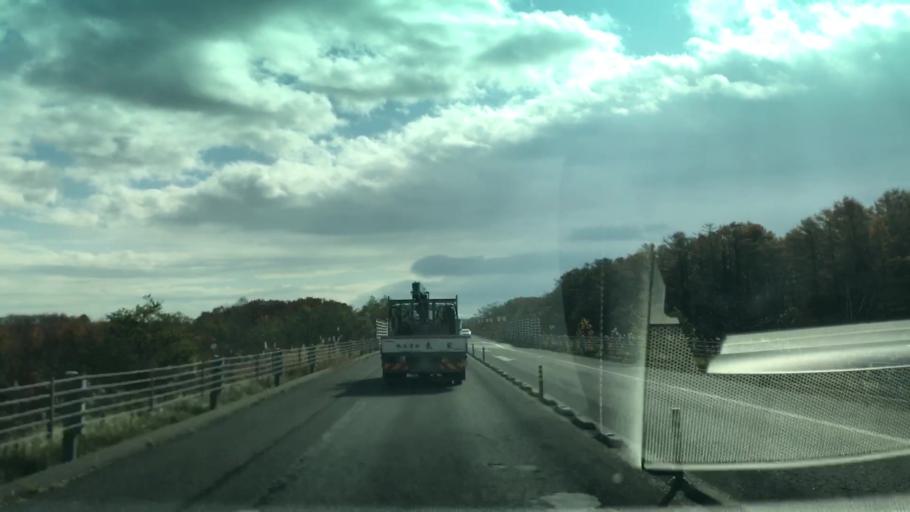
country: JP
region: Hokkaido
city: Tomakomai
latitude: 42.5698
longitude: 141.9759
